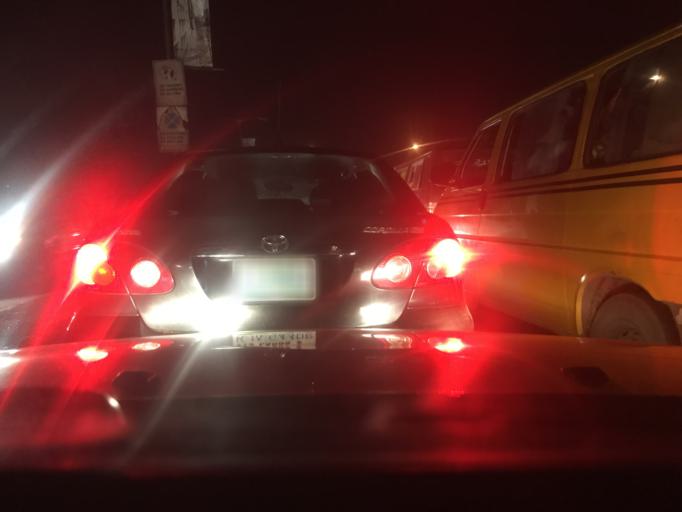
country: NG
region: Lagos
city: Agege
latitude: 6.5986
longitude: 3.2910
